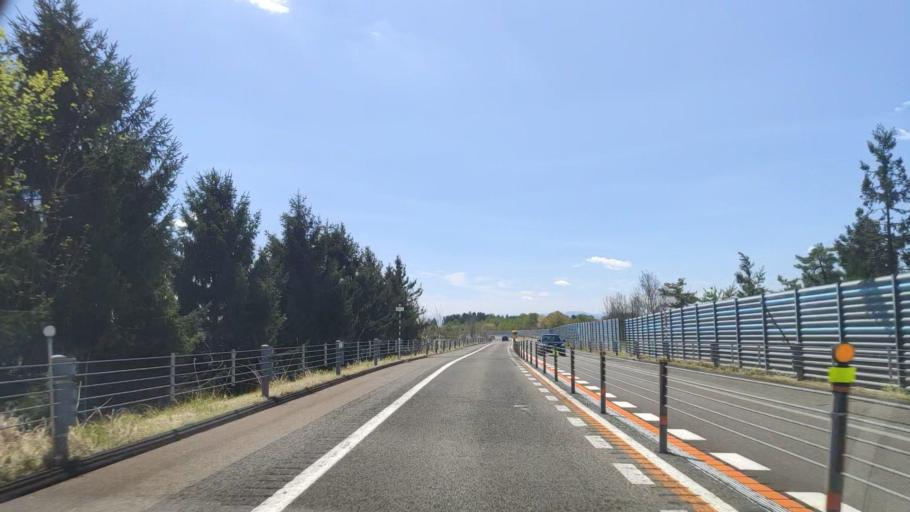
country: JP
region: Akita
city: Yokotemachi
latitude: 39.3516
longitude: 140.4969
